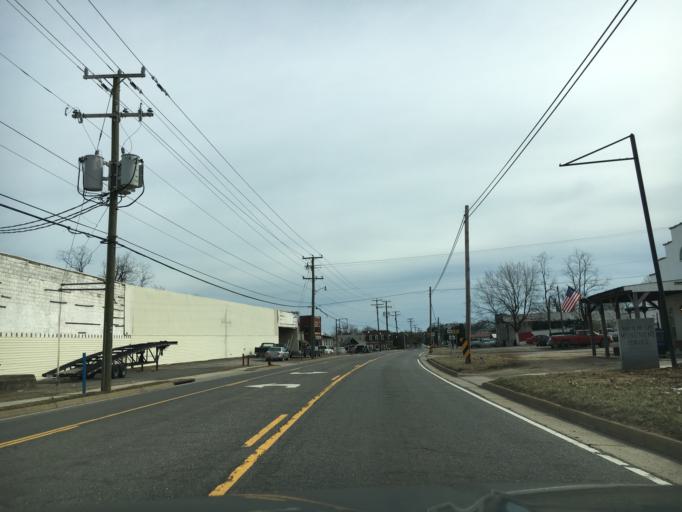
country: US
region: Virginia
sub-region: Appomattox County
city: Appomattox
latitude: 37.3589
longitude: -78.8275
